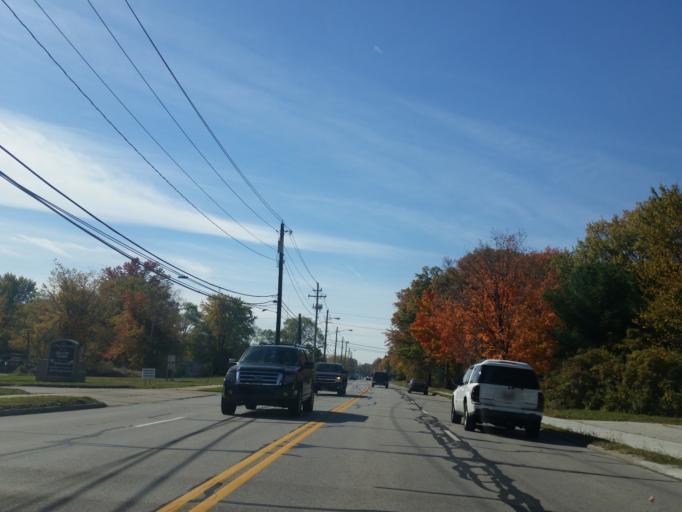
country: US
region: Ohio
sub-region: Cuyahoga County
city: Westlake
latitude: 41.4518
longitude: -81.9162
